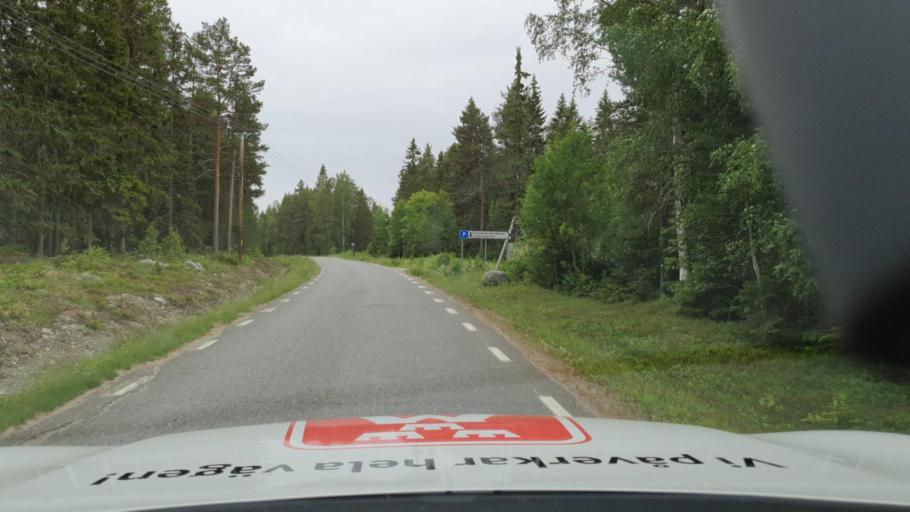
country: SE
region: Vaesterbotten
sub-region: Nordmalings Kommun
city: Nordmaling
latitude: 63.4370
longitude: 19.4699
